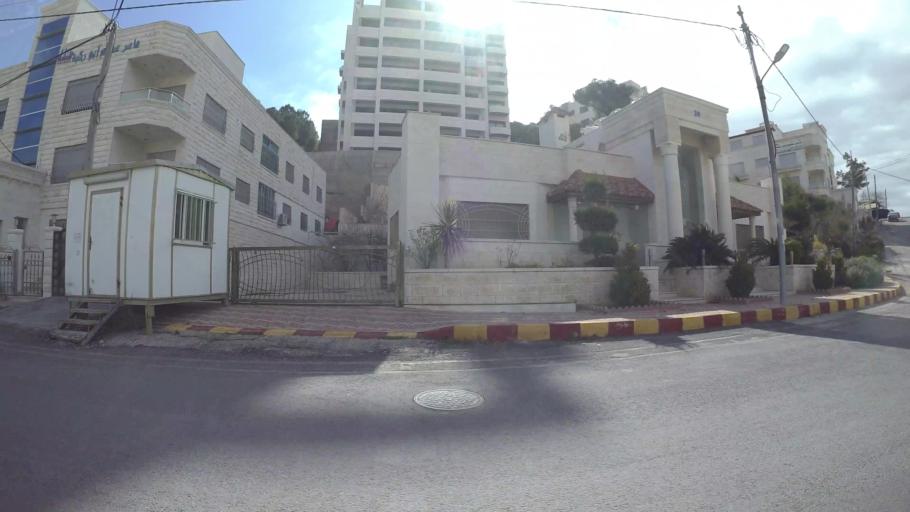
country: JO
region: Amman
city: Al Jubayhah
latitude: 32.0105
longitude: 35.8409
